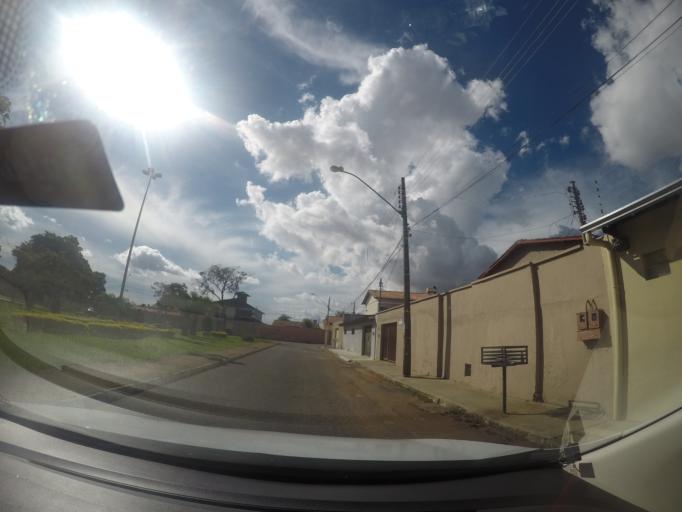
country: BR
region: Goias
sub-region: Goiania
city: Goiania
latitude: -16.6804
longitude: -49.3006
